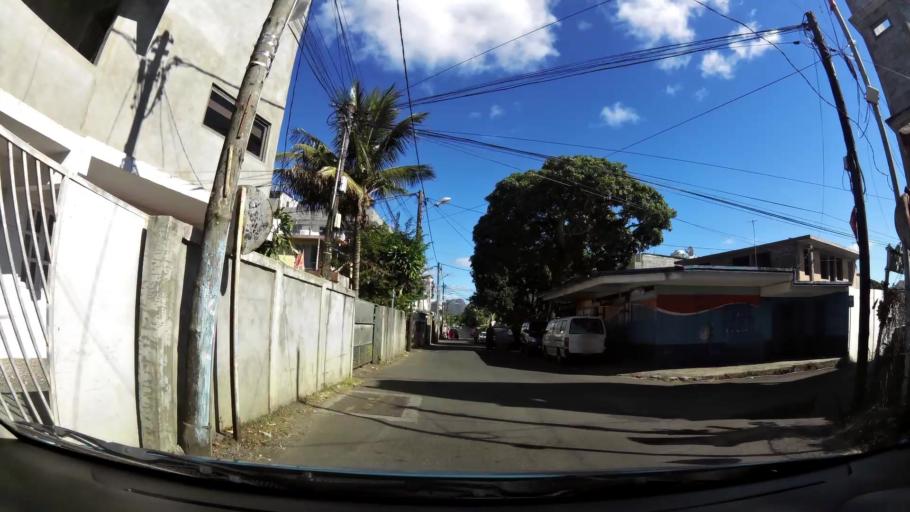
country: MU
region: Plaines Wilhems
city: Quatre Bornes
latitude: -20.2731
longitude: 57.4732
